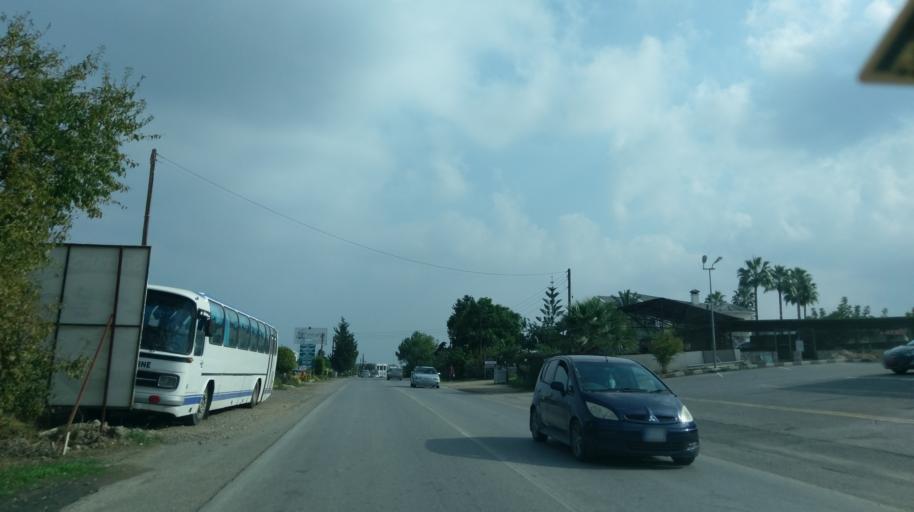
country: CY
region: Keryneia
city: Kyrenia
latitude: 35.3250
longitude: 33.4030
